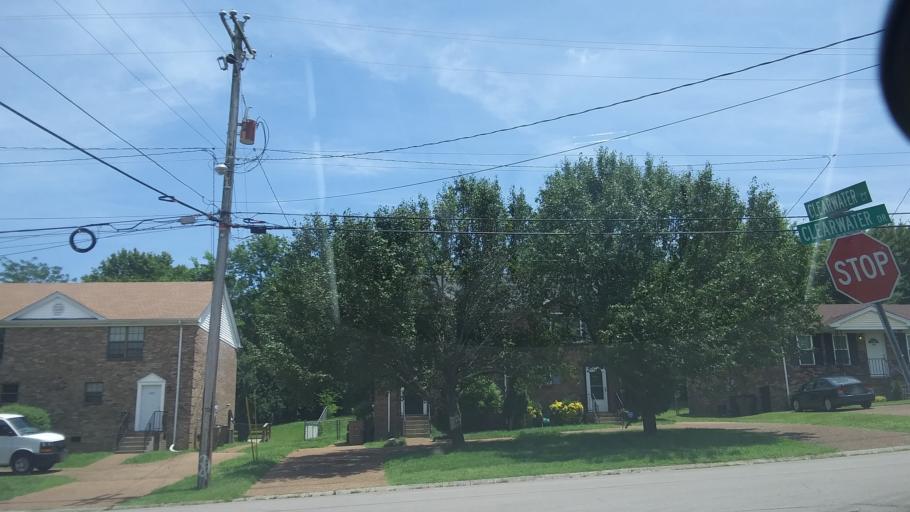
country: US
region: Tennessee
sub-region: Rutherford County
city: La Vergne
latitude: 36.0770
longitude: -86.6295
